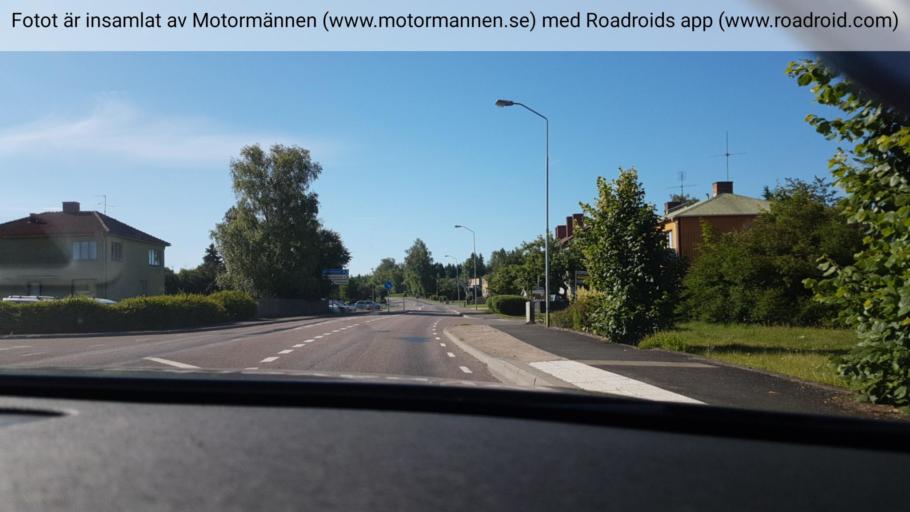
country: SE
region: Vaestra Goetaland
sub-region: Falkopings Kommun
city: Falkoeping
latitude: 58.0744
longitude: 13.5208
